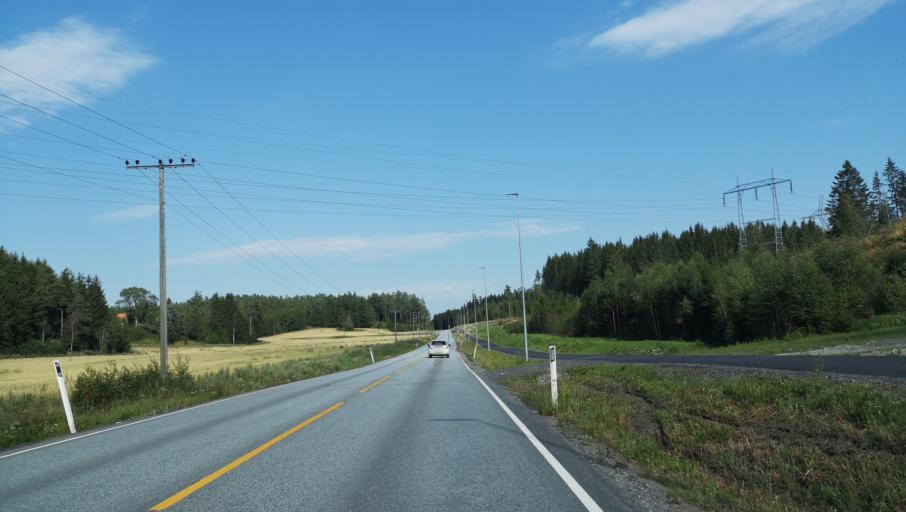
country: NO
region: Ostfold
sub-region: Valer
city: Kirkebygda
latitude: 59.4905
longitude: 10.8118
